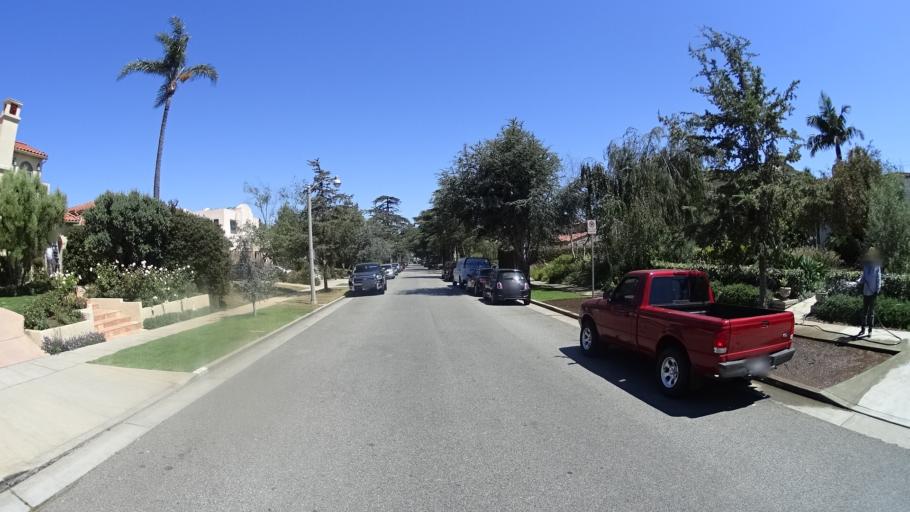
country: US
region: California
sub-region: Los Angeles County
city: Santa Monica
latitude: 34.0391
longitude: -118.4928
